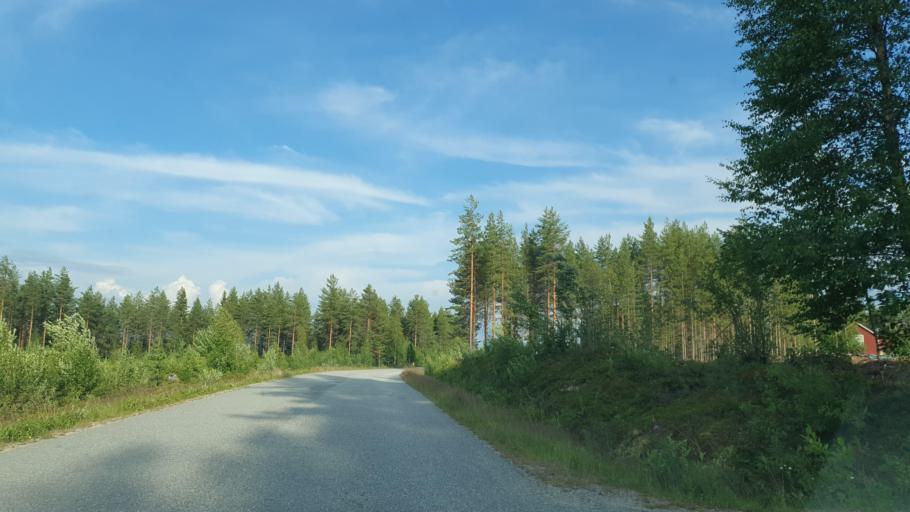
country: FI
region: Kainuu
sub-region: Kehys-Kainuu
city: Kuhmo
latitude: 64.3118
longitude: 29.5386
